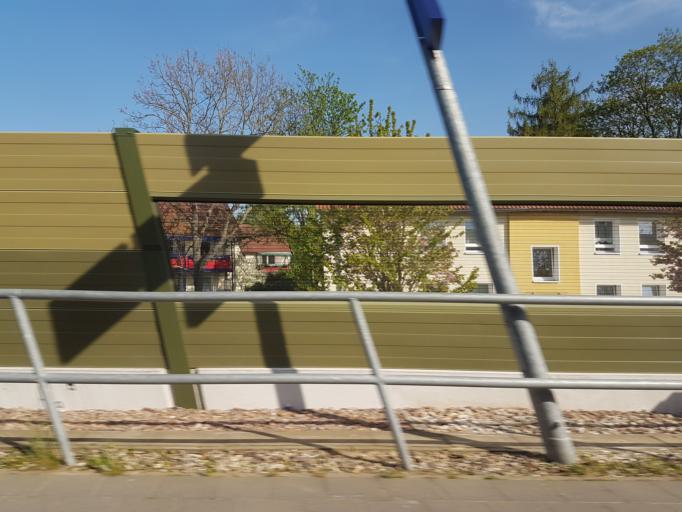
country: DE
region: Lower Saxony
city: Ronnenberg
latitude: 52.3408
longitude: 9.6698
